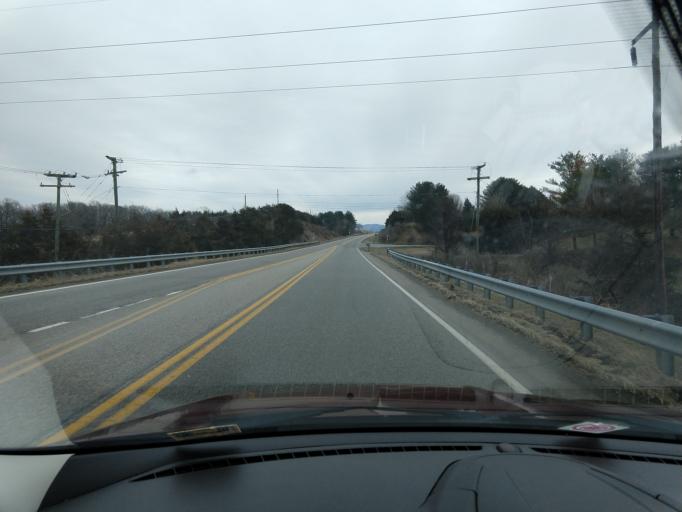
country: US
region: Virginia
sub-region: Augusta County
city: Weyers Cave
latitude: 38.2825
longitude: -78.9064
